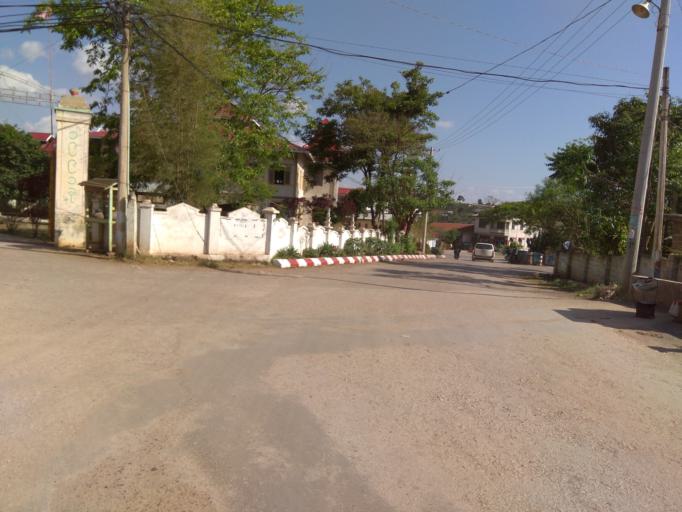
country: MM
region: Shan
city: Taunggyi
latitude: 20.6568
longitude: 96.6376
